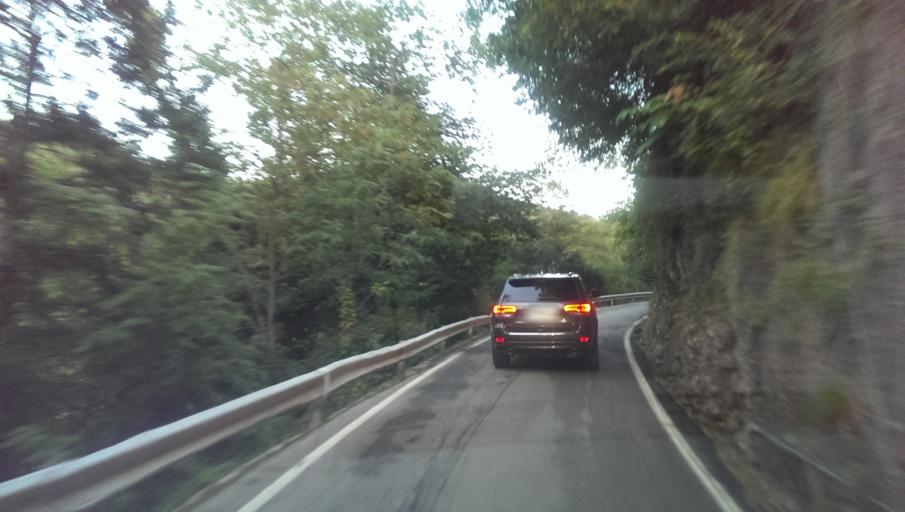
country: IT
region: Lombardy
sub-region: Provincia di Brescia
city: Pieve
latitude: 45.7776
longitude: 10.7572
